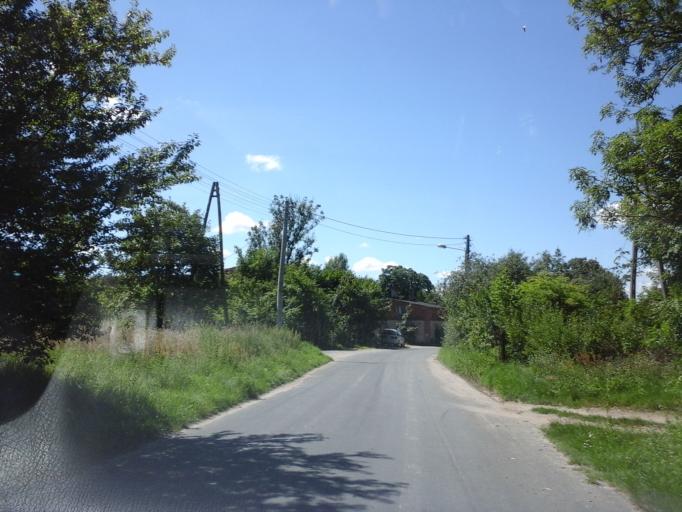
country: PL
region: West Pomeranian Voivodeship
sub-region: Powiat choszczenski
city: Recz
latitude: 53.2925
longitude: 15.5023
